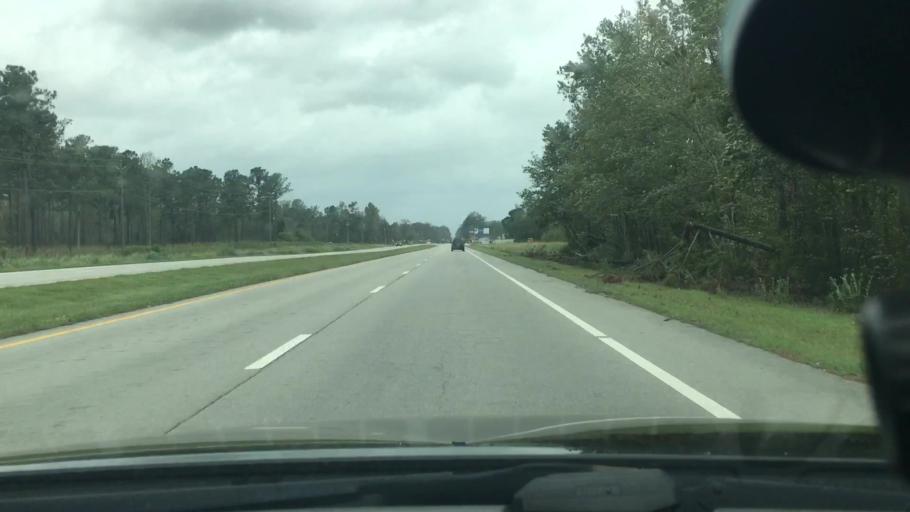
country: US
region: North Carolina
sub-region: Craven County
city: New Bern
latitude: 35.1488
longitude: -77.0330
